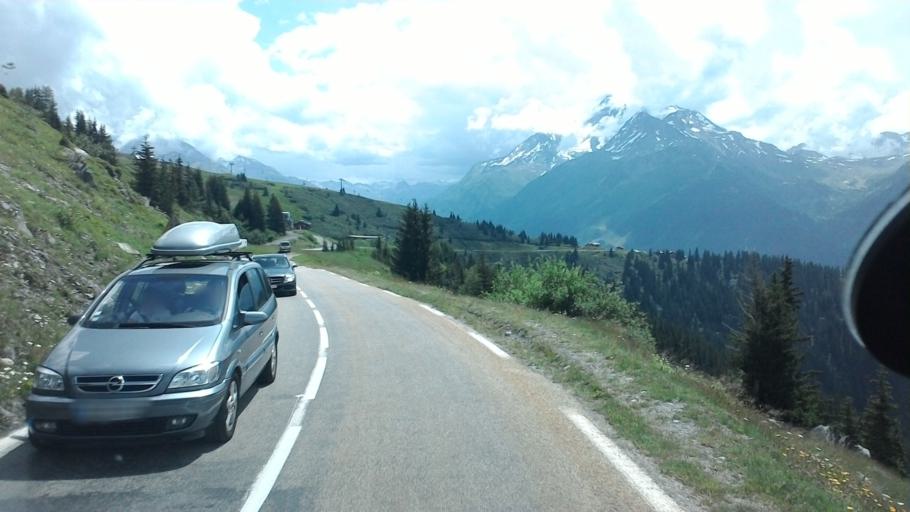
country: FR
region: Rhone-Alpes
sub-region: Departement de la Savoie
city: Seez
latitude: 45.6404
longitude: 6.8453
